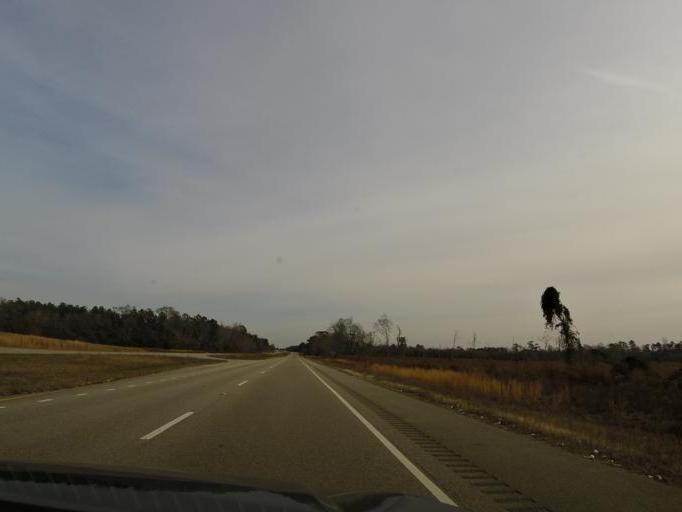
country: US
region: Alabama
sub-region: Houston County
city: Ashford
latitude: 31.1342
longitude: -85.1213
